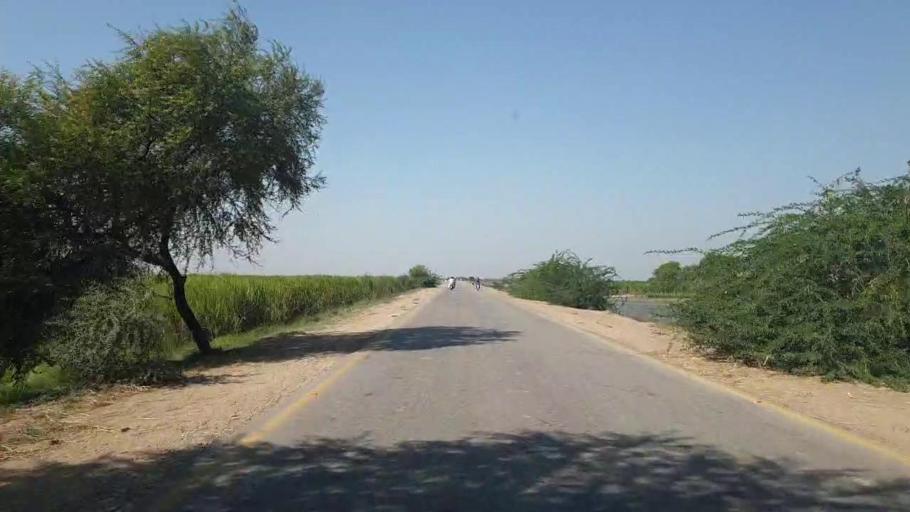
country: PK
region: Sindh
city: Rajo Khanani
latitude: 25.0121
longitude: 68.8329
